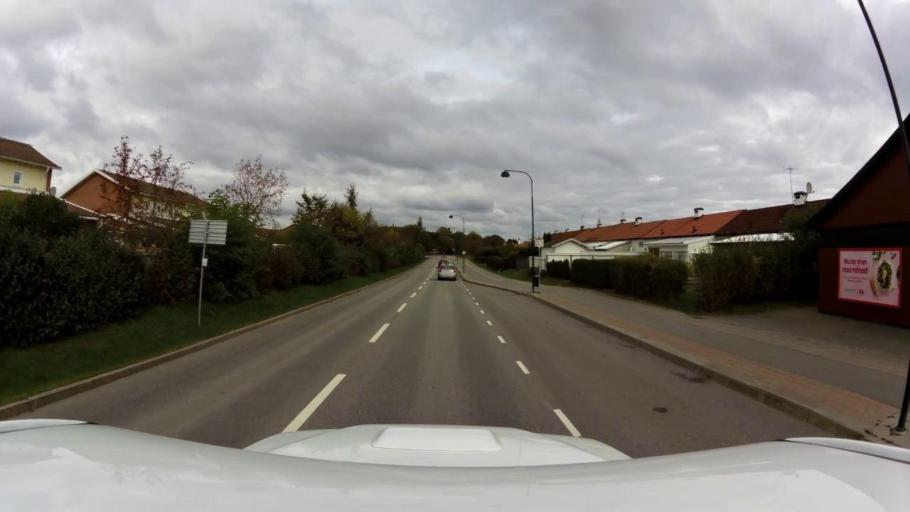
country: SE
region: OEstergoetland
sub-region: Linkopings Kommun
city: Berg
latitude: 58.4893
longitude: 15.5261
